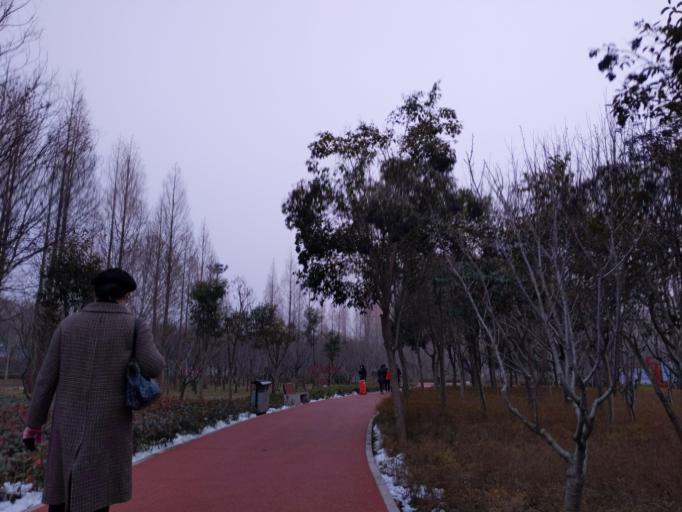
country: CN
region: Henan Sheng
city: Puyang
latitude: 35.7790
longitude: 115.0272
